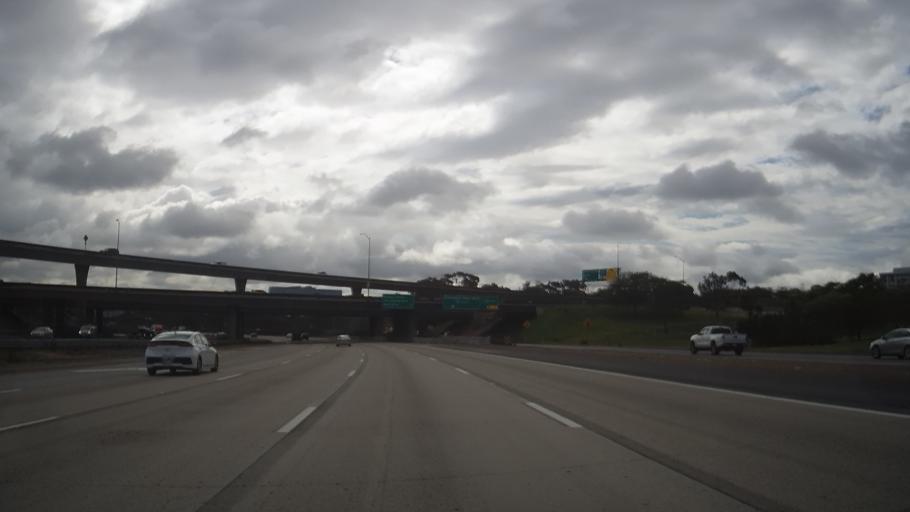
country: US
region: California
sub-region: San Diego County
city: La Mesa
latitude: 32.8443
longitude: -117.1205
